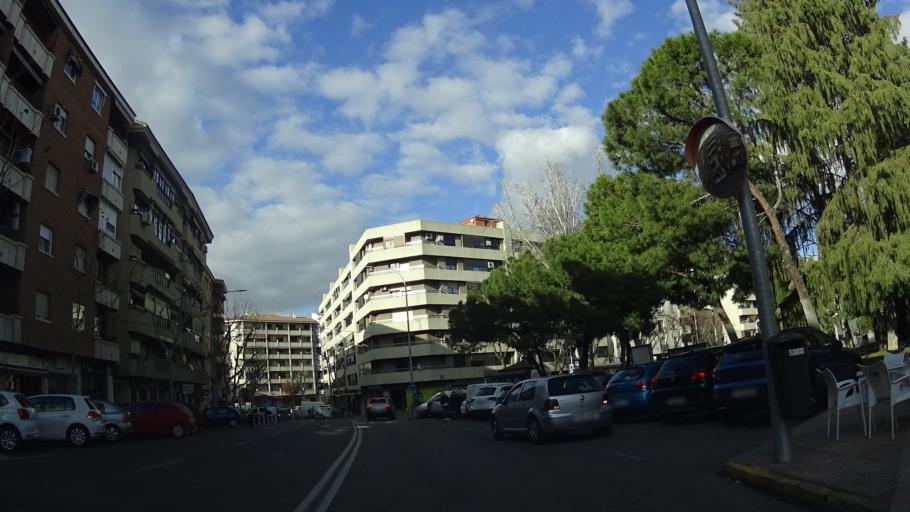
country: ES
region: Castille-La Mancha
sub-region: Provincia de Ciudad Real
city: Ciudad Real
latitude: 38.9836
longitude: -3.9252
